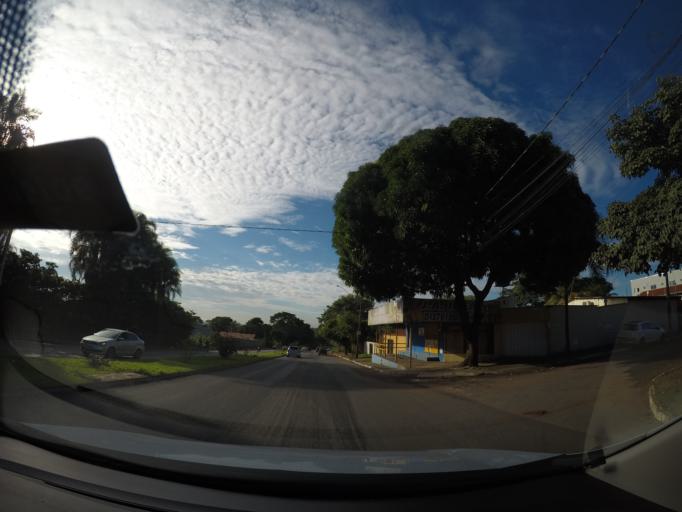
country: BR
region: Goias
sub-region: Goiania
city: Goiania
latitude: -16.7434
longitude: -49.2704
